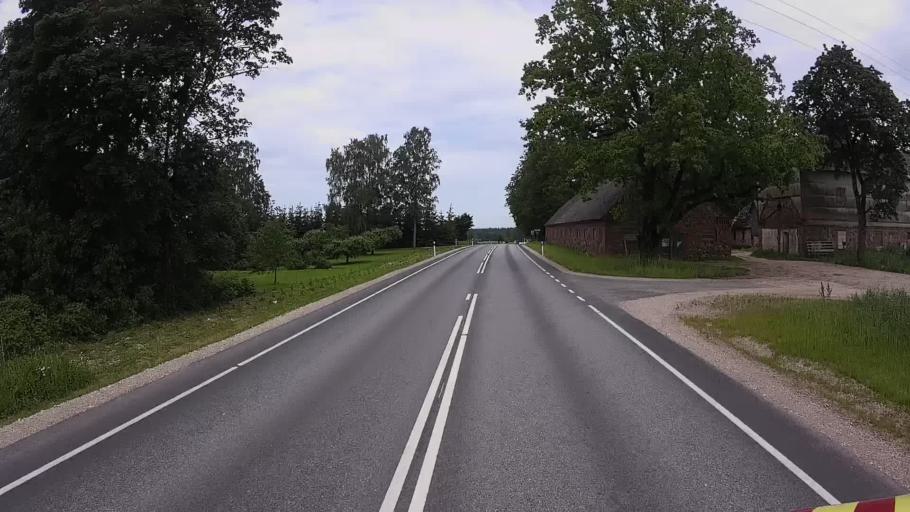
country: EE
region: Viljandimaa
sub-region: Viljandi linn
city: Viljandi
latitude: 58.2714
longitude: 25.5835
